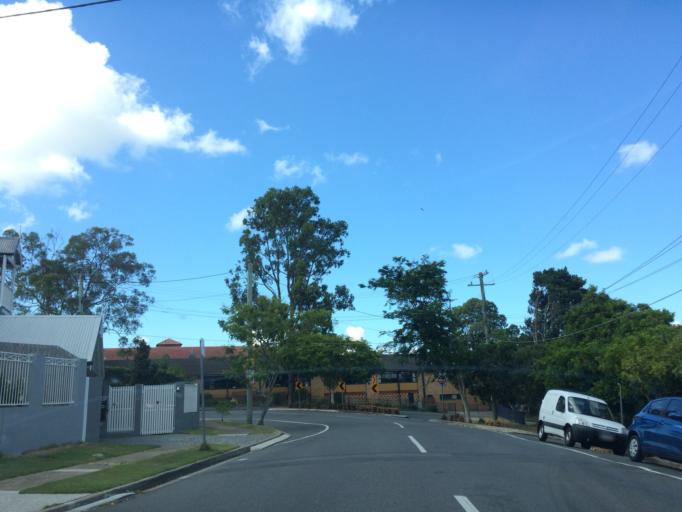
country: AU
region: Queensland
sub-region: Brisbane
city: Woolloongabba
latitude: -27.4852
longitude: 153.0506
